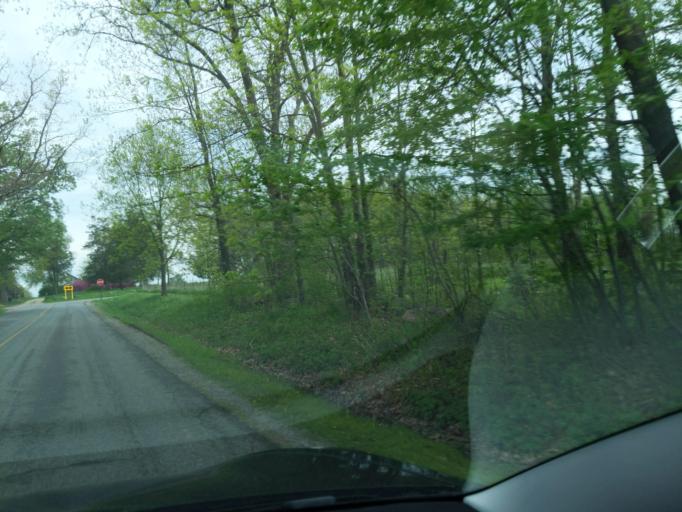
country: US
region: Michigan
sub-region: Ingham County
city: Stockbridge
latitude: 42.4256
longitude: -84.2583
